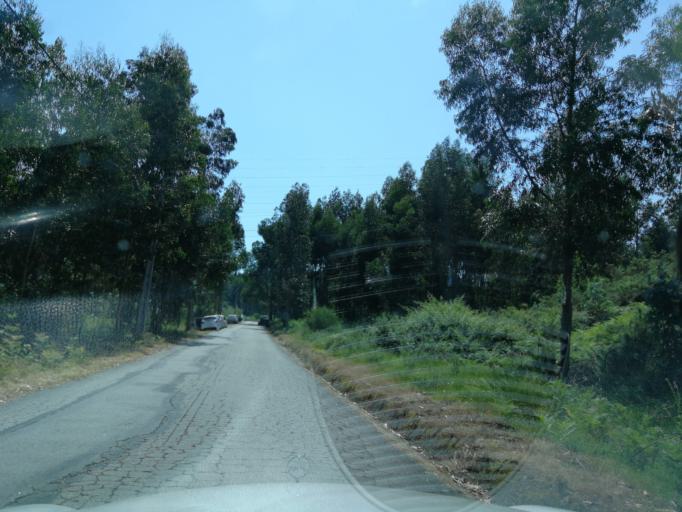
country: PT
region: Braga
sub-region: Povoa de Lanhoso
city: Povoa de Lanhoso
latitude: 41.5818
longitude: -8.3202
